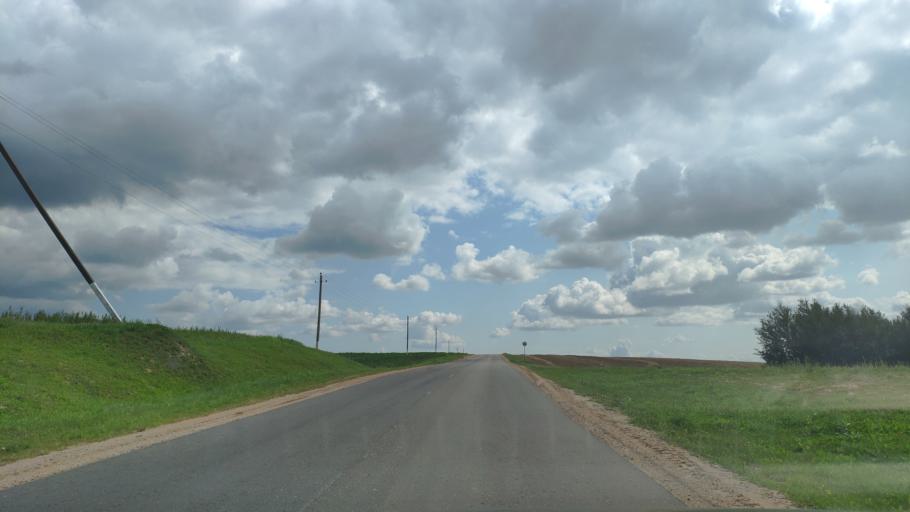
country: BY
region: Minsk
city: Khatsyezhyna
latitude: 53.8509
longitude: 27.3103
